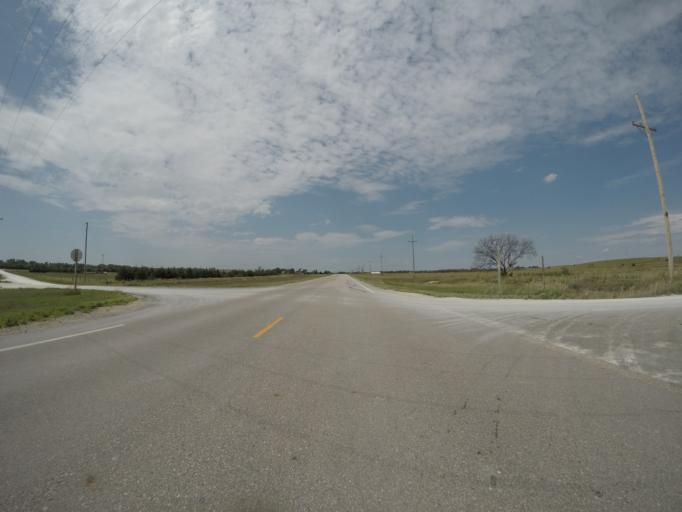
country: US
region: Kansas
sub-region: Rooks County
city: Stockton
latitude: 39.4405
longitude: -99.2494
